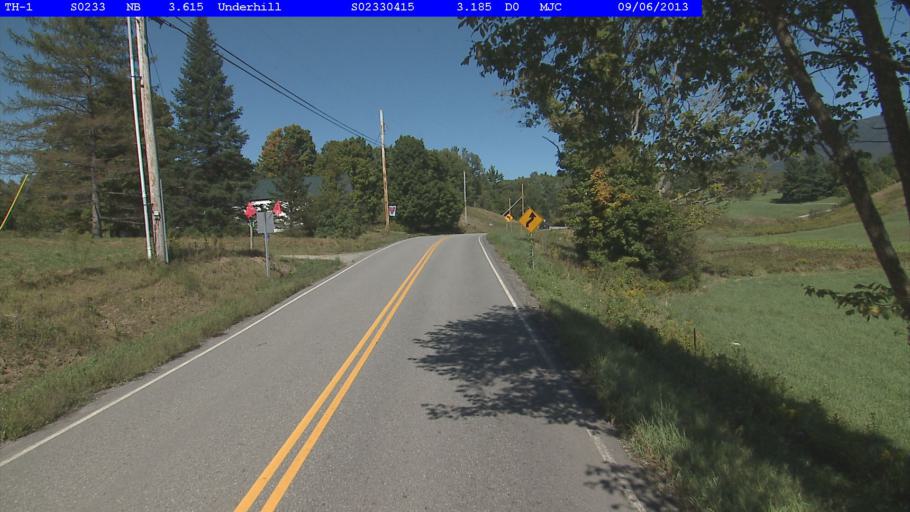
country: US
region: Vermont
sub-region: Chittenden County
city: Jericho
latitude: 44.5141
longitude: -72.8864
